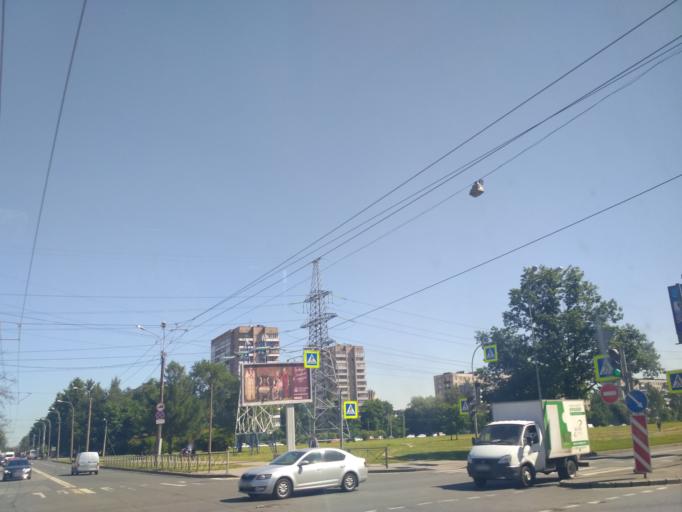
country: RU
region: Leningrad
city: Kalininskiy
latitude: 59.9776
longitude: 30.3930
